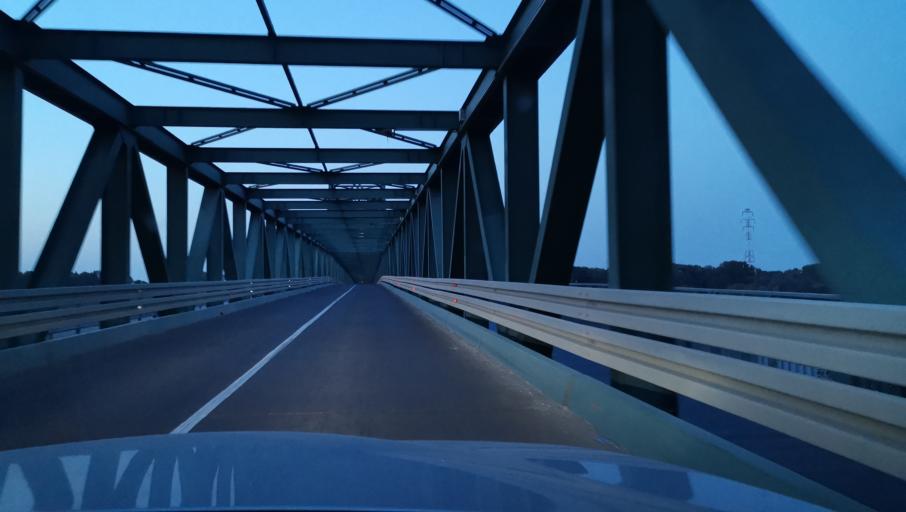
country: RS
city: Zvecka
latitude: 44.6714
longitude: 20.1655
